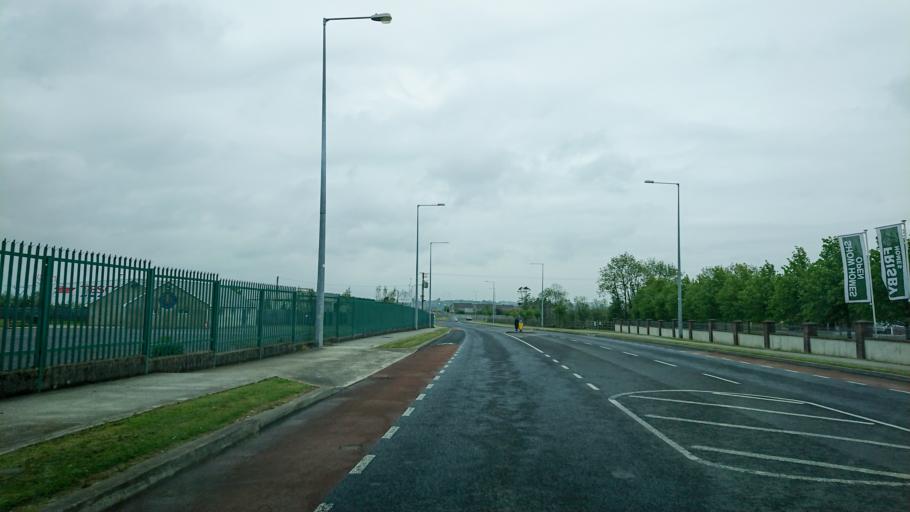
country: IE
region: Munster
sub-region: Waterford
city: Waterford
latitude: 52.2353
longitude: -7.1394
